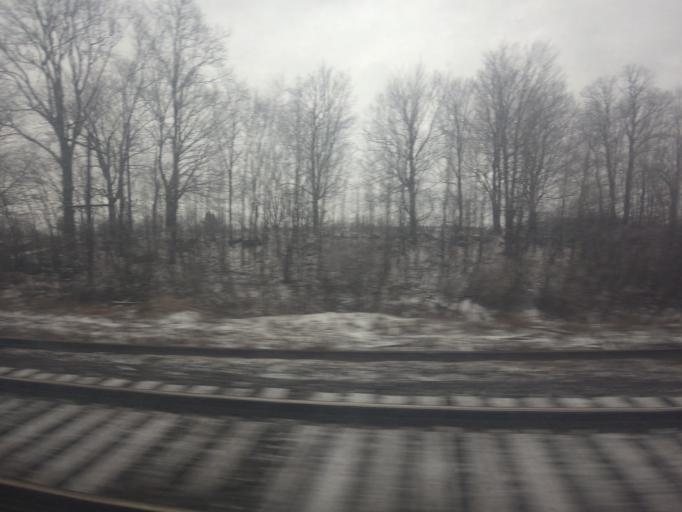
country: CA
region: Ontario
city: Gananoque
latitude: 44.3642
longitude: -76.1713
